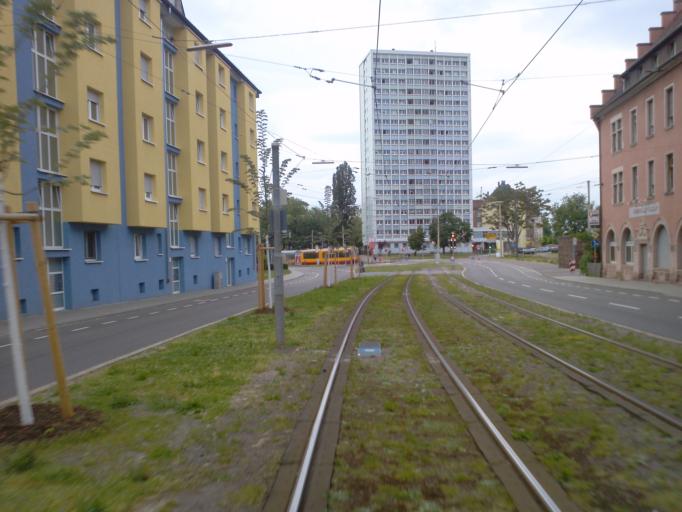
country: DE
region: Baden-Wuerttemberg
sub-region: Karlsruhe Region
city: Karlsruhe
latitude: 49.0122
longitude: 8.3560
